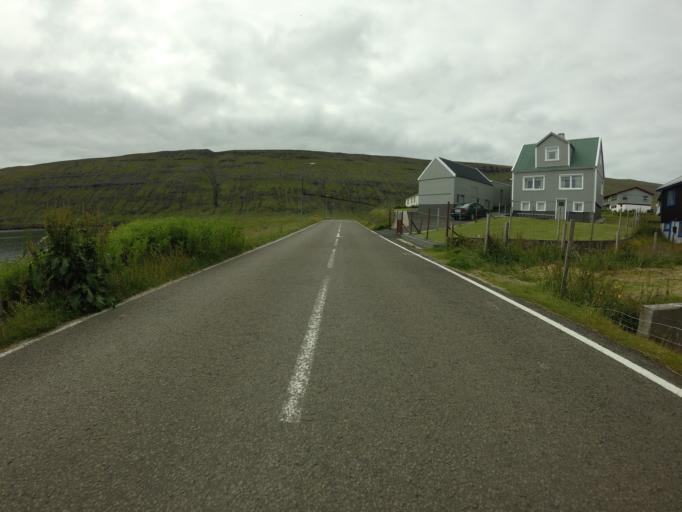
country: FO
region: Suduroy
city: Tvoroyri
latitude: 61.6317
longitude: -6.9290
